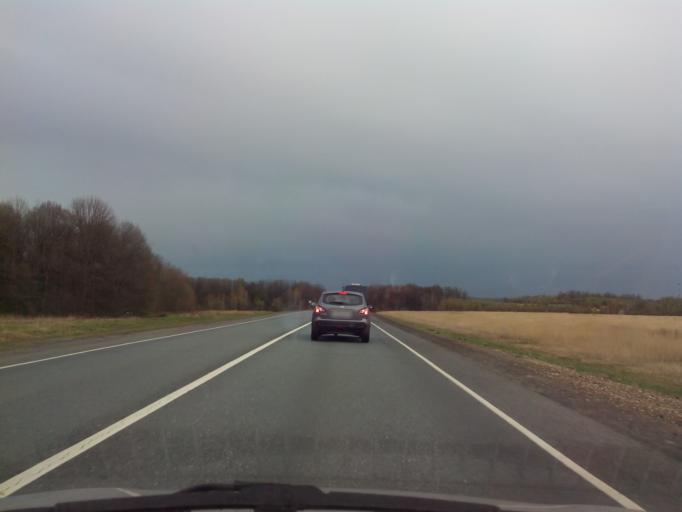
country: RU
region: Moskovskaya
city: Uzunovo
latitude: 54.5504
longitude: 38.4647
